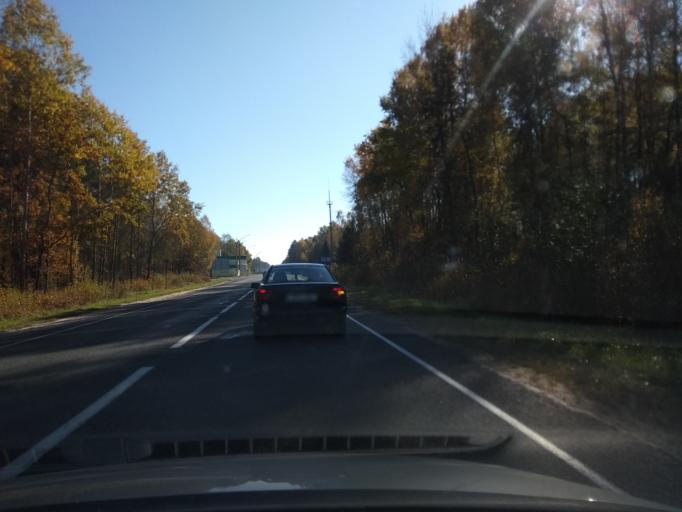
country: BY
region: Brest
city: Malaryta
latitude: 51.8936
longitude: 24.1369
